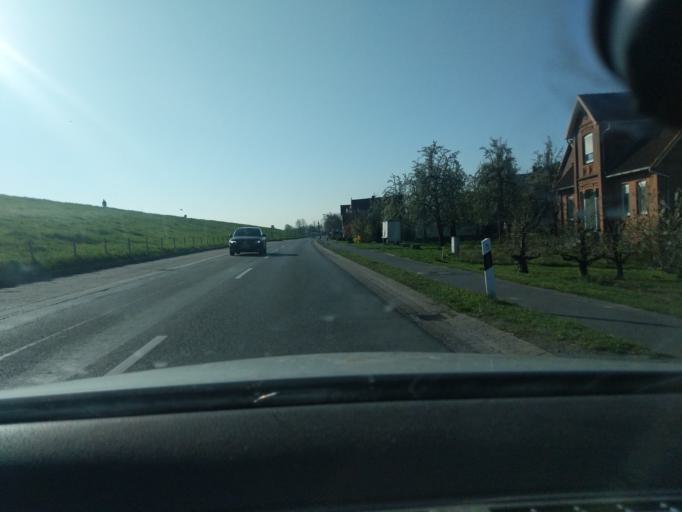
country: DE
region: Lower Saxony
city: Mittelnkirchen
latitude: 53.5650
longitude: 9.6504
